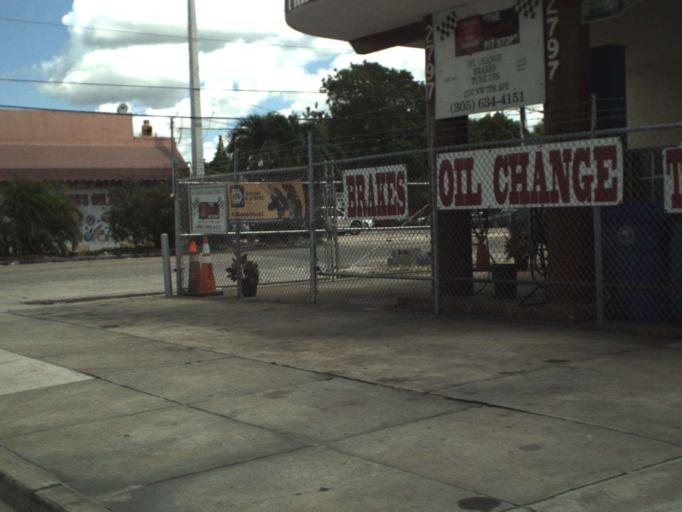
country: US
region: Florida
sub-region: Miami-Dade County
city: Allapattah
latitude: 25.8024
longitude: -80.2072
